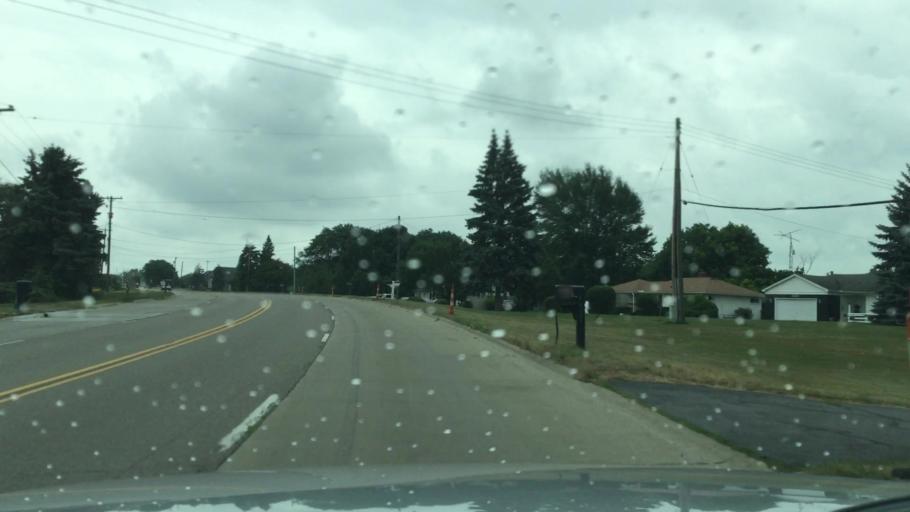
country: US
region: Michigan
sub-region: Genesee County
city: Flint
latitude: 43.0212
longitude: -83.7552
